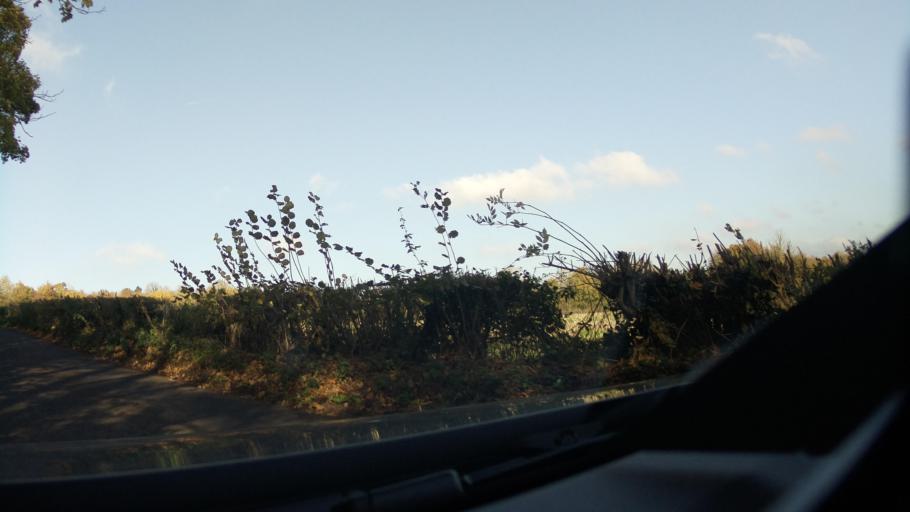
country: GB
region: England
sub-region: Somerset
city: Frome
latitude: 51.2084
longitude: -2.3350
